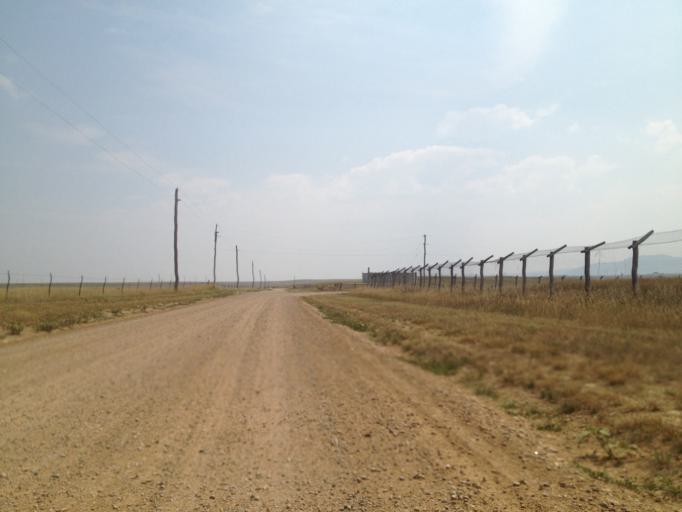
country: US
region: Colorado
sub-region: Boulder County
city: Superior
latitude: 39.9441
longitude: -105.1988
